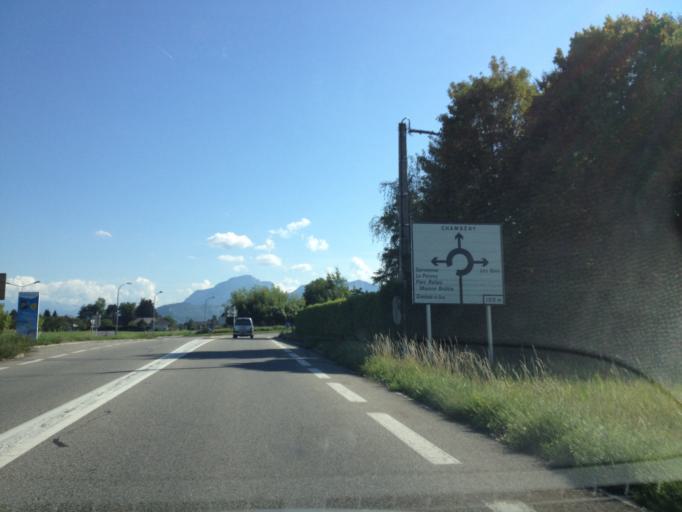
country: FR
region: Rhone-Alpes
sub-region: Departement de la Savoie
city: Sonnaz
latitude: 45.6106
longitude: 5.9105
